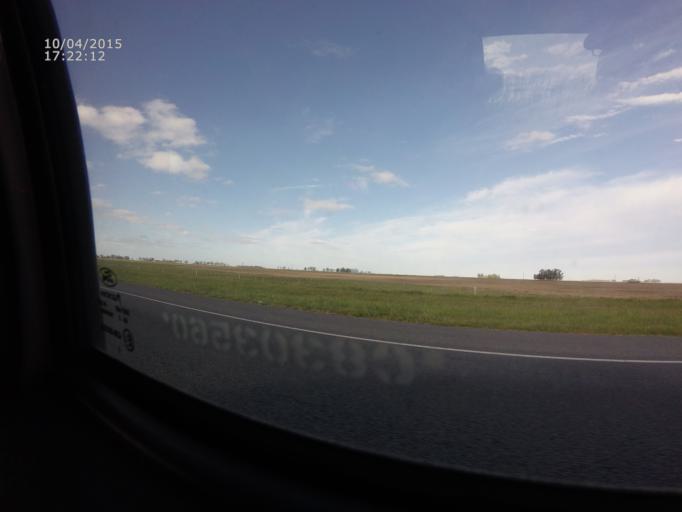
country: AR
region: Buenos Aires
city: Maipu
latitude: -37.1195
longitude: -57.8221
